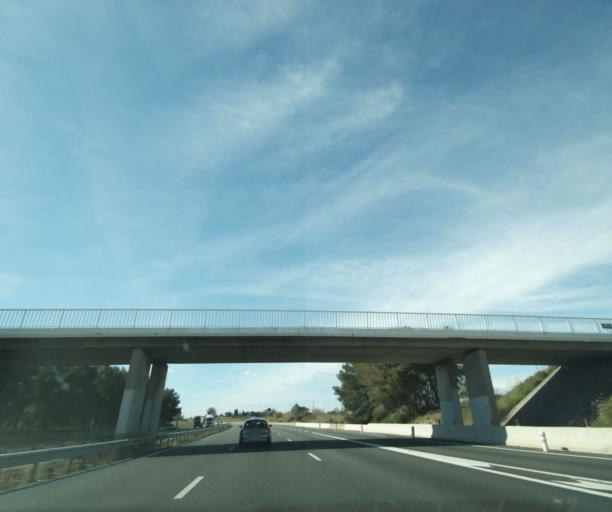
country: FR
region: Languedoc-Roussillon
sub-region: Departement de l'Herault
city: Loupian
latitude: 43.4503
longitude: 3.5860
